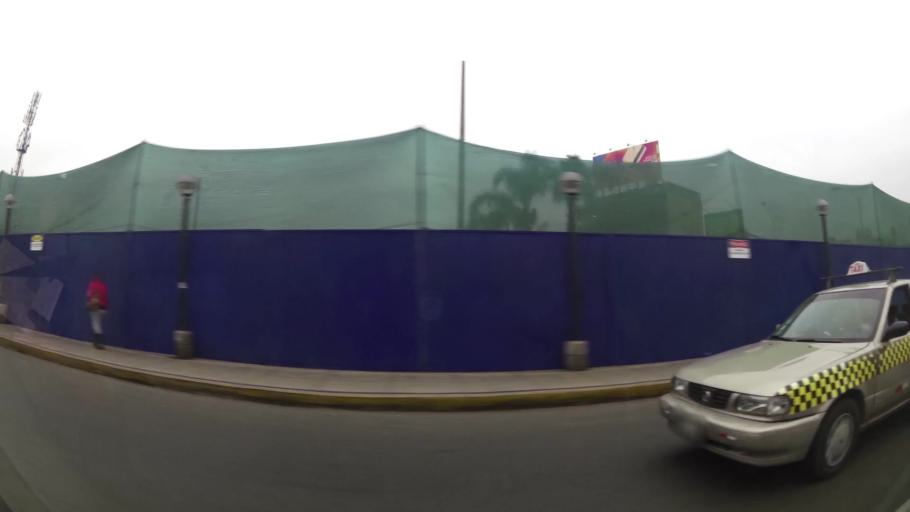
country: PE
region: Lima
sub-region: Lima
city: San Isidro
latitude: -12.0761
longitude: -77.0639
